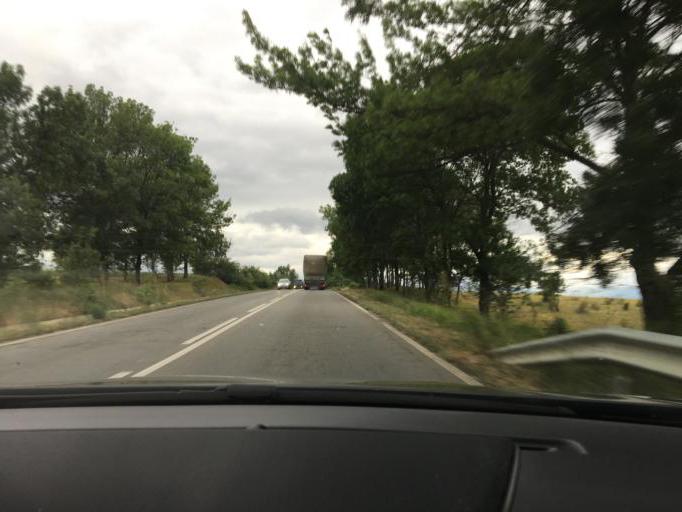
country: BG
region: Kyustendil
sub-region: Obshtina Kyustendil
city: Kyustendil
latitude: 42.2712
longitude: 22.7780
